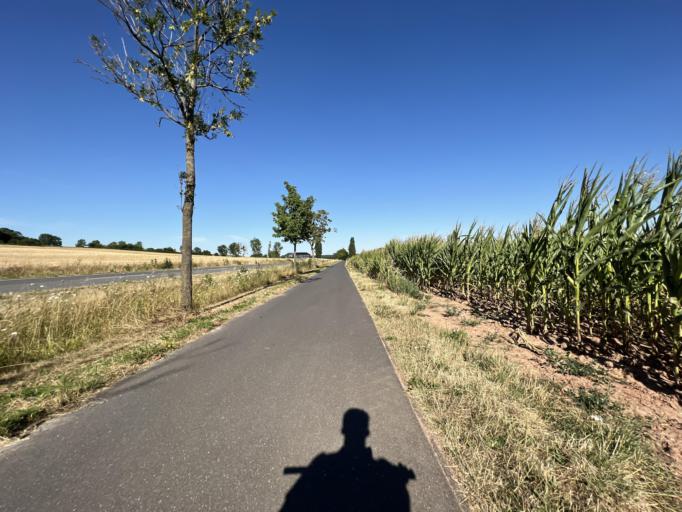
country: DE
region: North Rhine-Westphalia
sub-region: Regierungsbezirk Koln
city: Kreuzau
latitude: 50.7526
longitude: 6.4544
